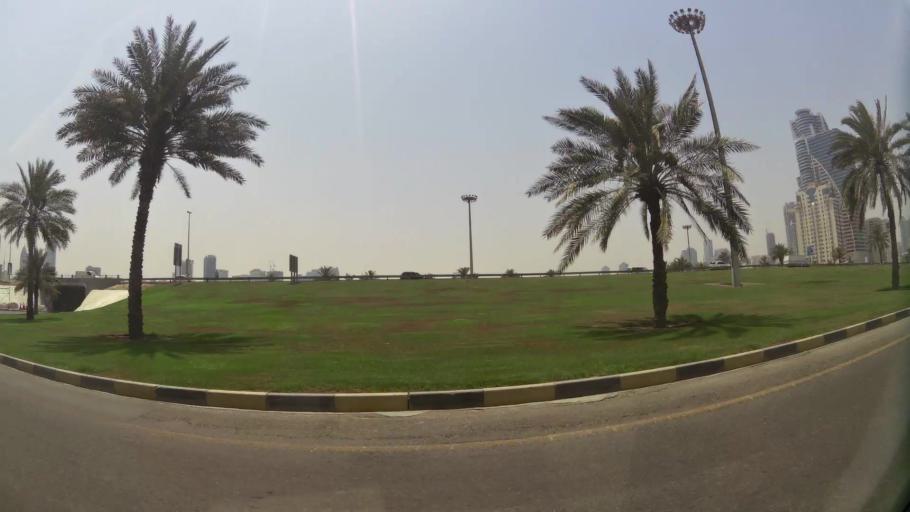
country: AE
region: Ash Shariqah
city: Sharjah
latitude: 25.3414
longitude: 55.3762
